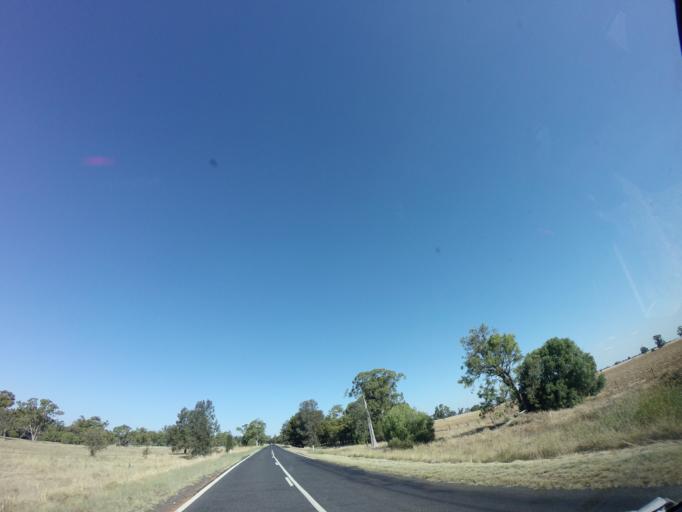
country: AU
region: New South Wales
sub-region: Gilgandra
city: Gilgandra
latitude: -31.6601
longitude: 148.3424
